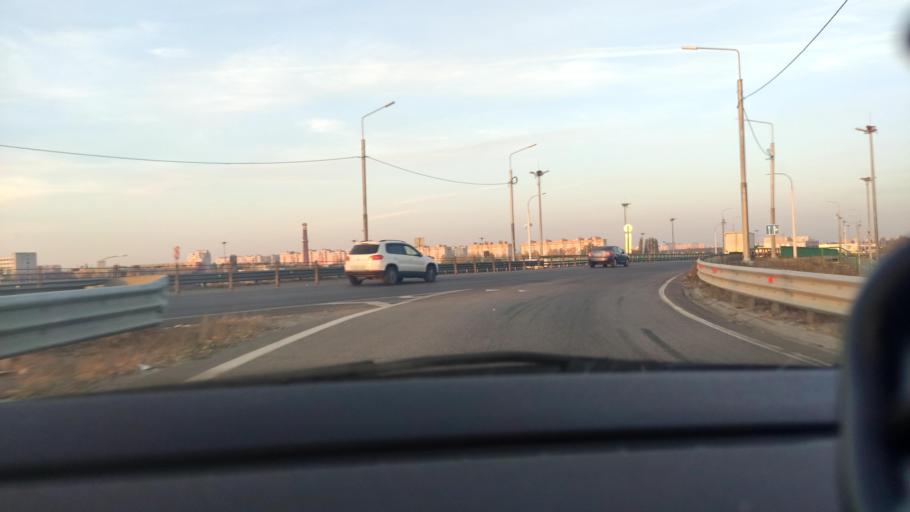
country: RU
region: Voronezj
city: Somovo
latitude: 51.6781
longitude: 39.3030
